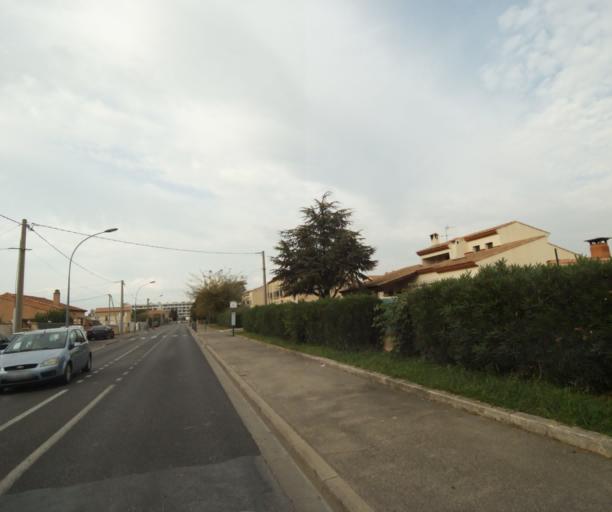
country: FR
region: Provence-Alpes-Cote d'Azur
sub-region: Departement des Bouches-du-Rhone
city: Marignane
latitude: 43.4059
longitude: 5.2155
